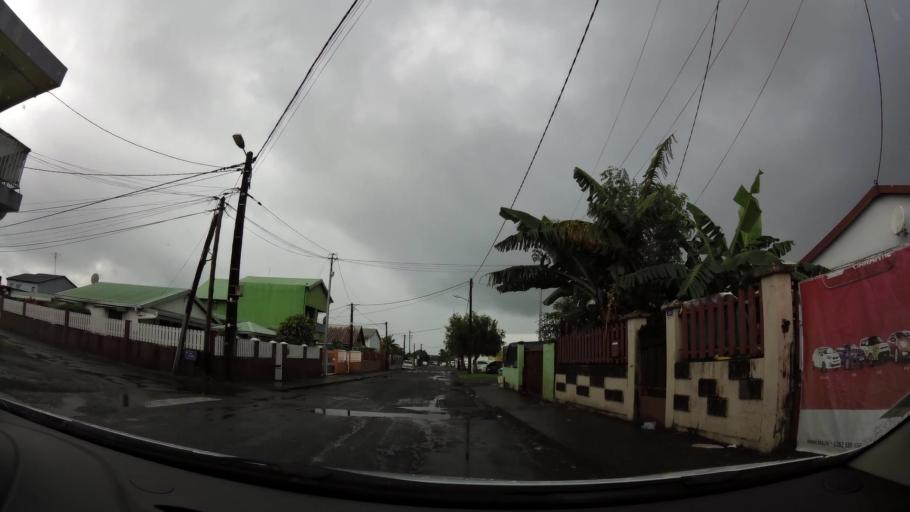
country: RE
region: Reunion
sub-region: Reunion
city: Saint-Andre
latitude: -20.9291
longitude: 55.6449
